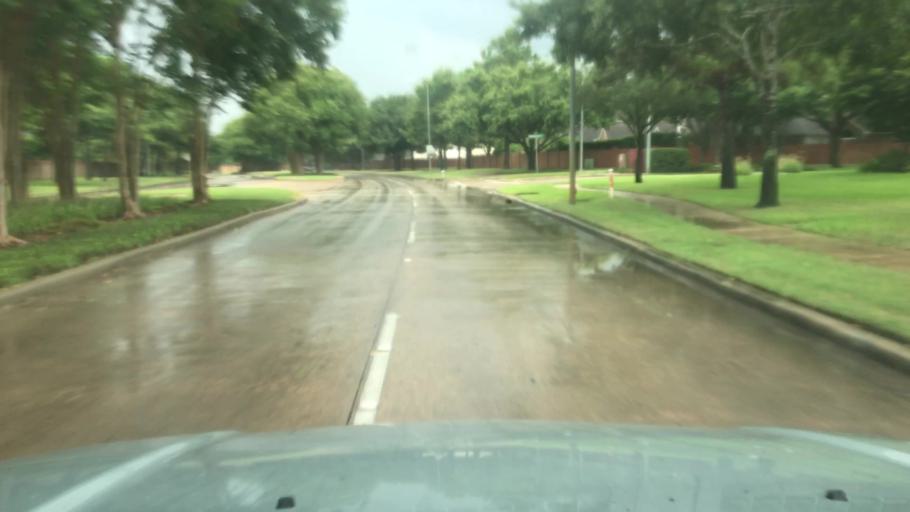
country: US
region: Texas
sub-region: Fort Bend County
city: Cinco Ranch
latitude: 29.7407
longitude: -95.7875
